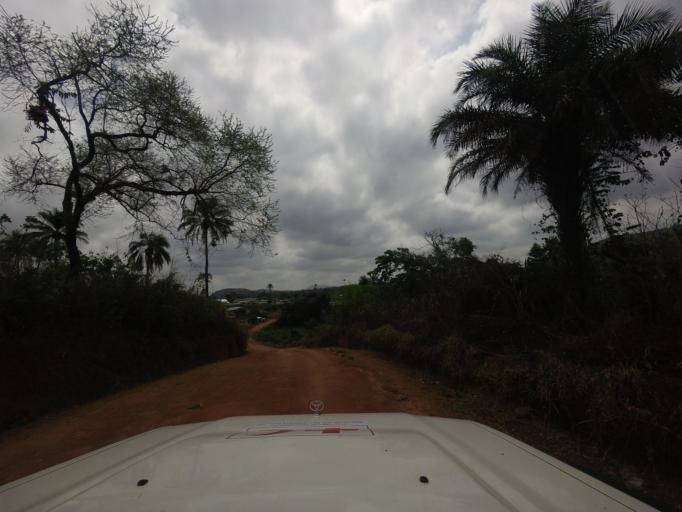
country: LR
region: Lofa
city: Voinjama
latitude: 8.4163
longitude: -9.7404
